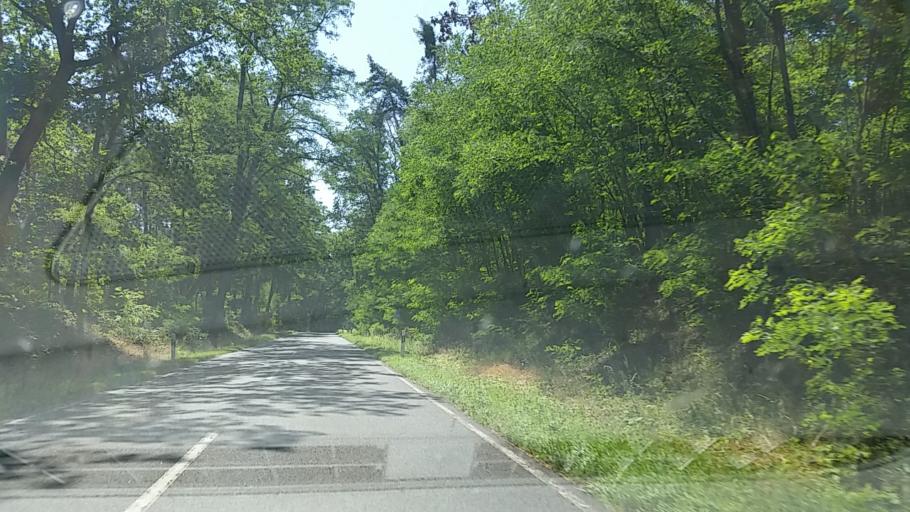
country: DE
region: Saxony-Anhalt
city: Pretzsch
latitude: 51.6836
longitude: 12.8017
